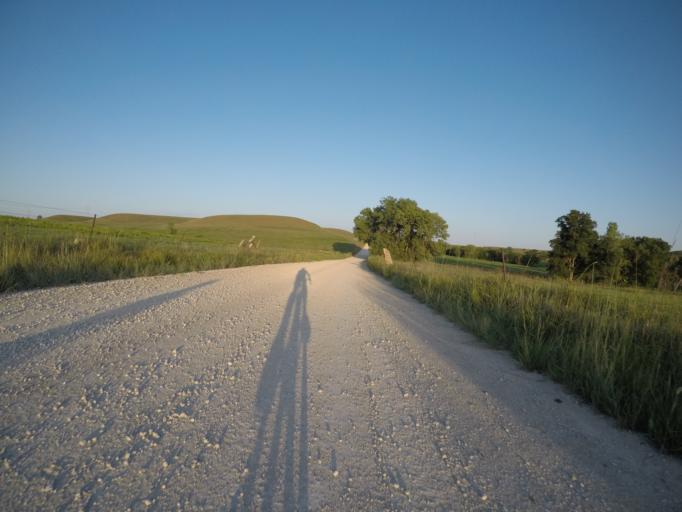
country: US
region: Kansas
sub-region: Riley County
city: Ogden
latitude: 39.0138
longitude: -96.6585
